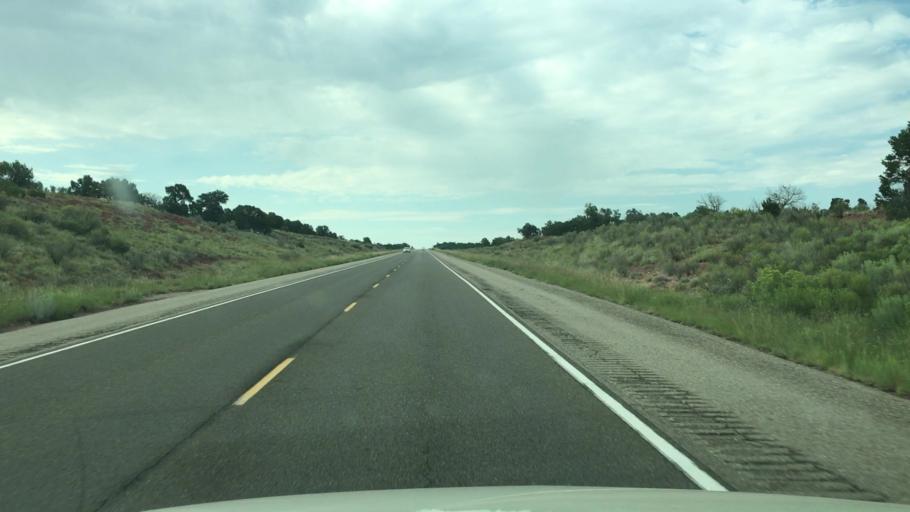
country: US
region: New Mexico
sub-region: Santa Fe County
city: Eldorado at Santa Fe
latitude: 35.2341
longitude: -105.8039
